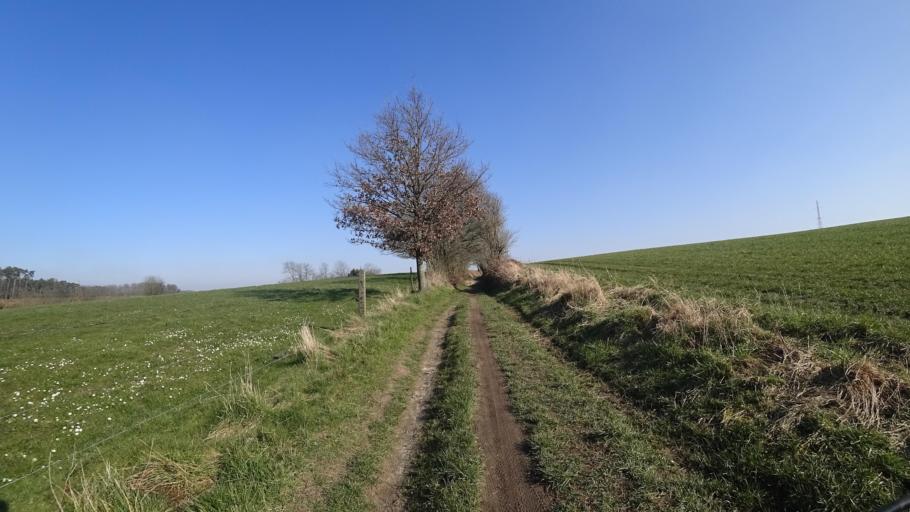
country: BE
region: Wallonia
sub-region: Province du Brabant Wallon
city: Court-Saint-Etienne
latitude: 50.6154
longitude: 4.5637
